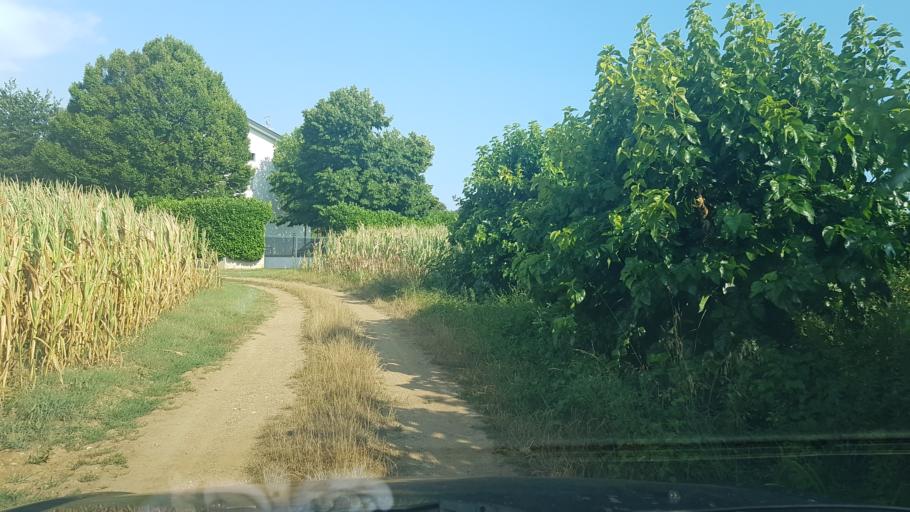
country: IT
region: Friuli Venezia Giulia
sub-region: Provincia di Udine
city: San Vito di Fagagna
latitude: 46.0603
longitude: 13.0833
